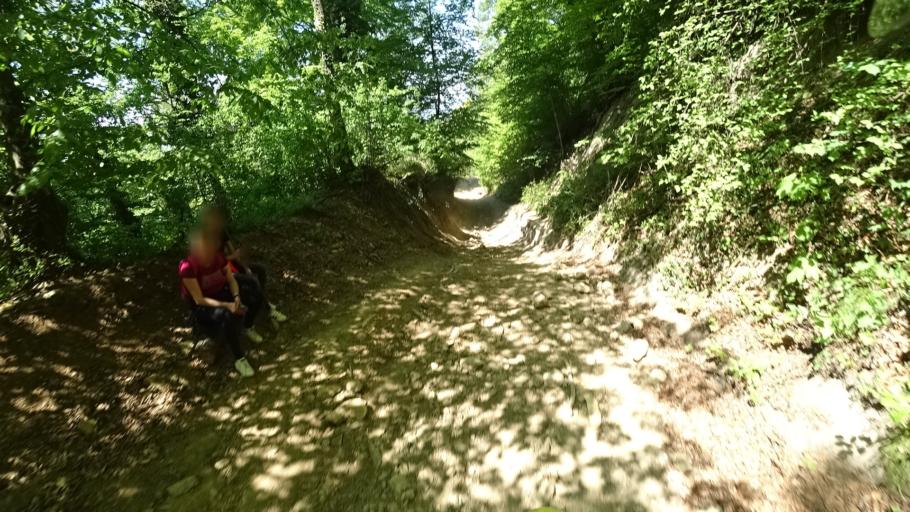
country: HR
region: Zagrebacka
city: Jablanovec
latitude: 45.8647
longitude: 15.8520
